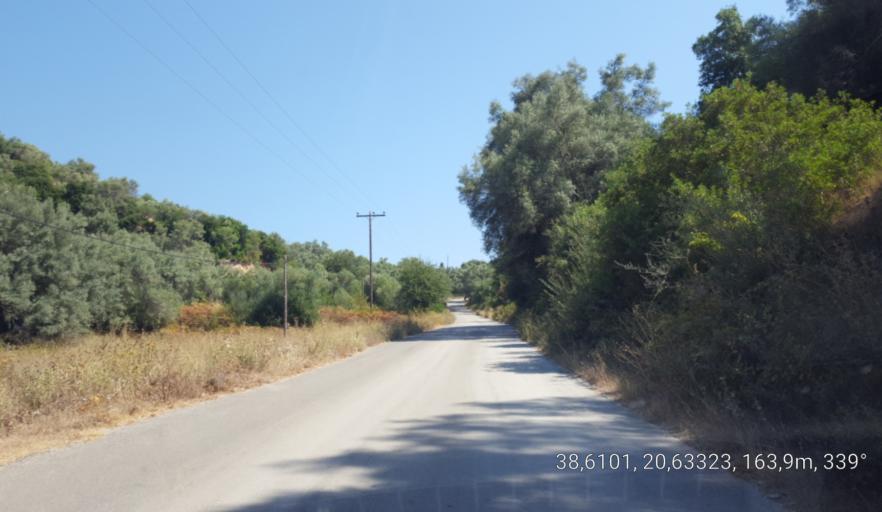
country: GR
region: Ionian Islands
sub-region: Lefkada
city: Nidri
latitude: 38.6101
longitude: 20.6332
